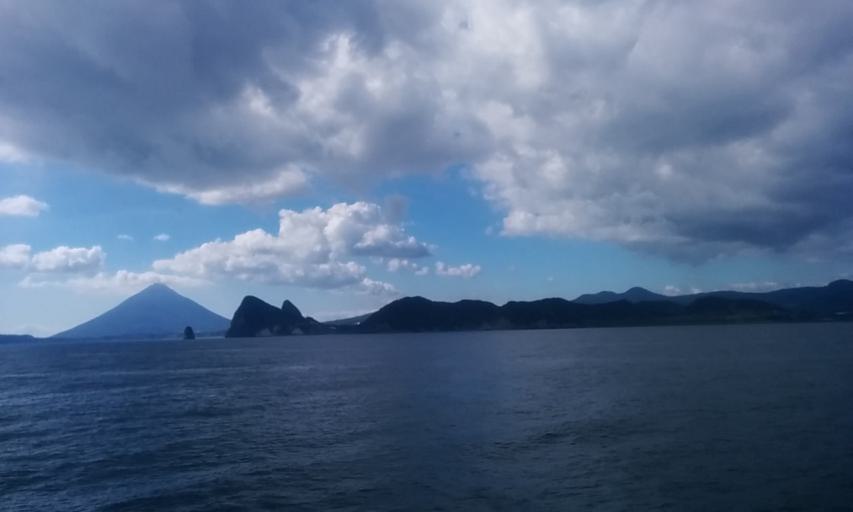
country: JP
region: Kagoshima
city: Ibusuki
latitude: 31.1777
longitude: 130.6662
